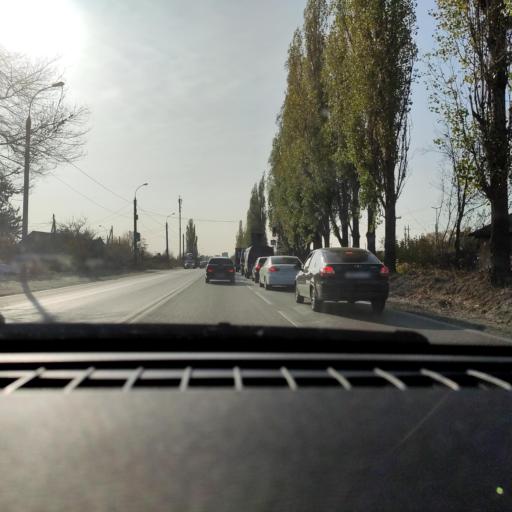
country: RU
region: Voronezj
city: Maslovka
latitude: 51.6178
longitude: 39.2585
